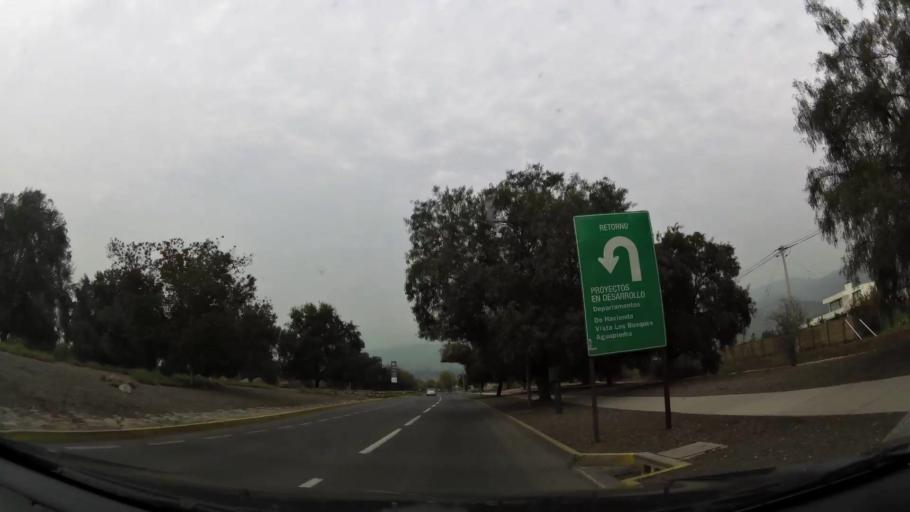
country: CL
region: Santiago Metropolitan
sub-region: Provincia de Chacabuco
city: Chicureo Abajo
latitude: -33.2811
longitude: -70.6363
